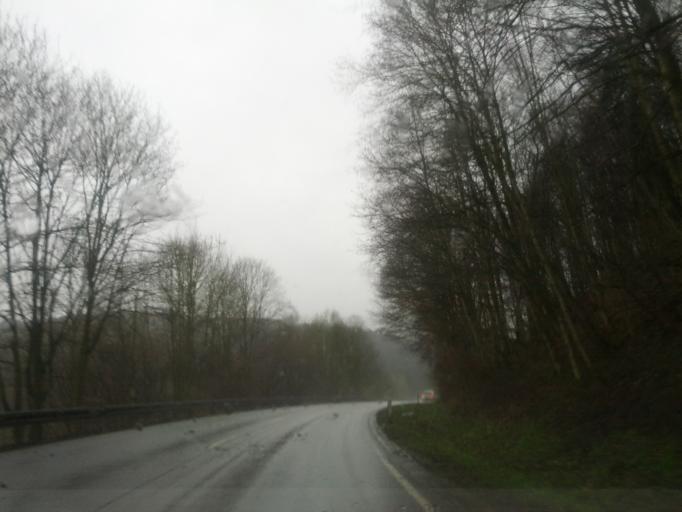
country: DE
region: Hesse
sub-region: Regierungsbezirk Kassel
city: Sontra
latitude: 51.0961
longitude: 9.9725
